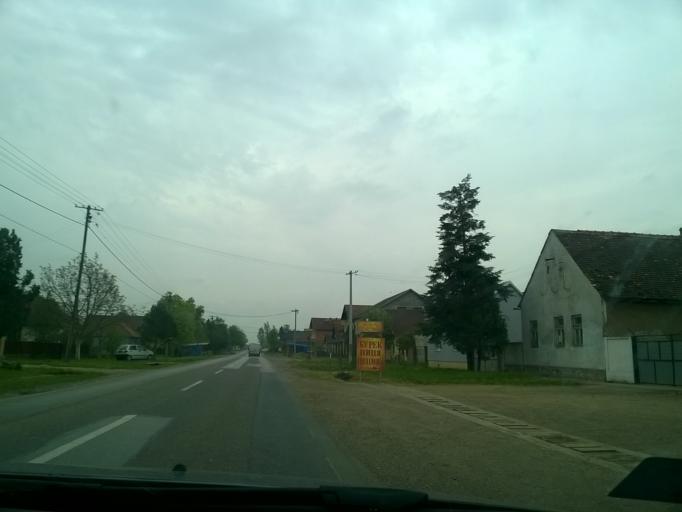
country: RS
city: Hrtkovci
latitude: 44.8714
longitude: 19.7700
